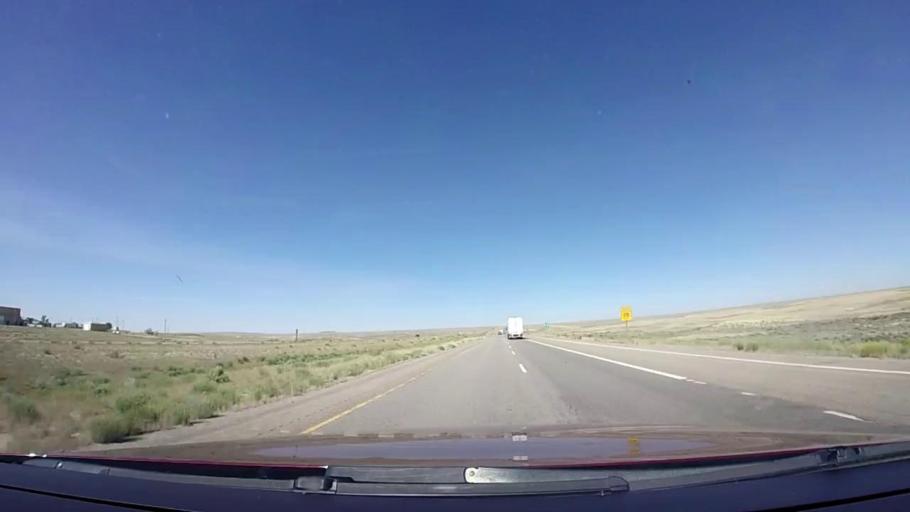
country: US
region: Wyoming
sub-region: Sweetwater County
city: Rock Springs
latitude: 41.6402
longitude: -108.4872
